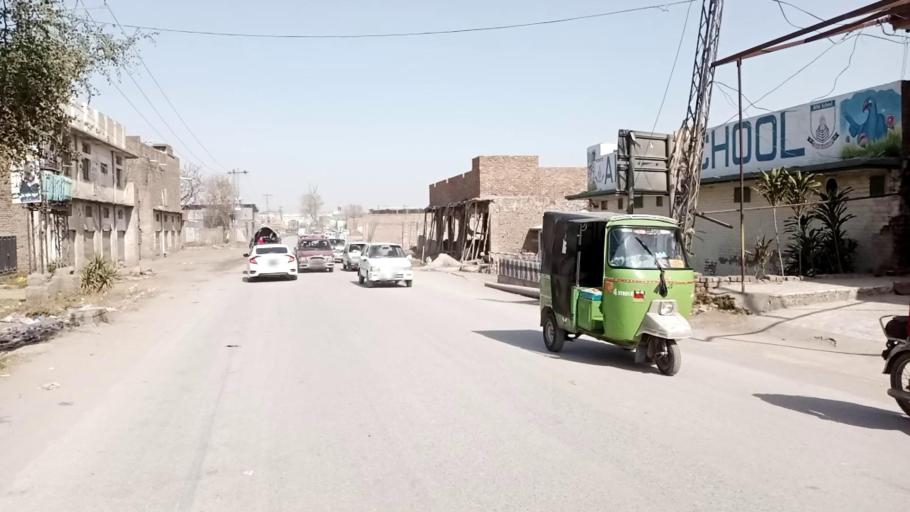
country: PK
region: Khyber Pakhtunkhwa
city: Peshawar
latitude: 34.0160
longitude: 71.6467
